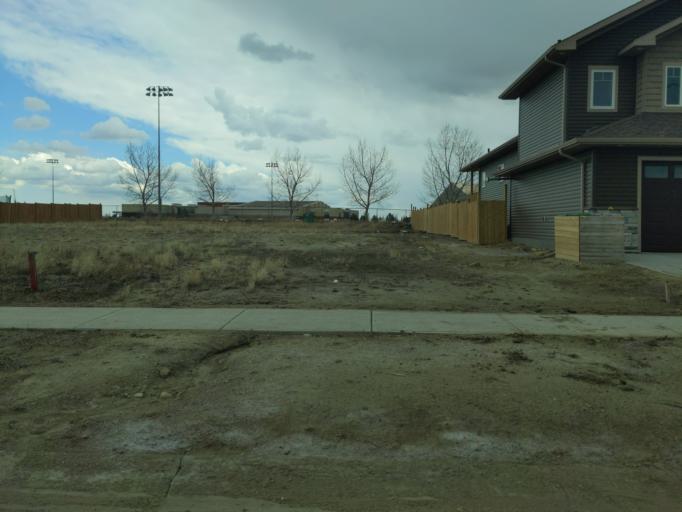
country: CA
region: Saskatchewan
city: Lloydminster
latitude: 53.2704
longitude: -110.0466
